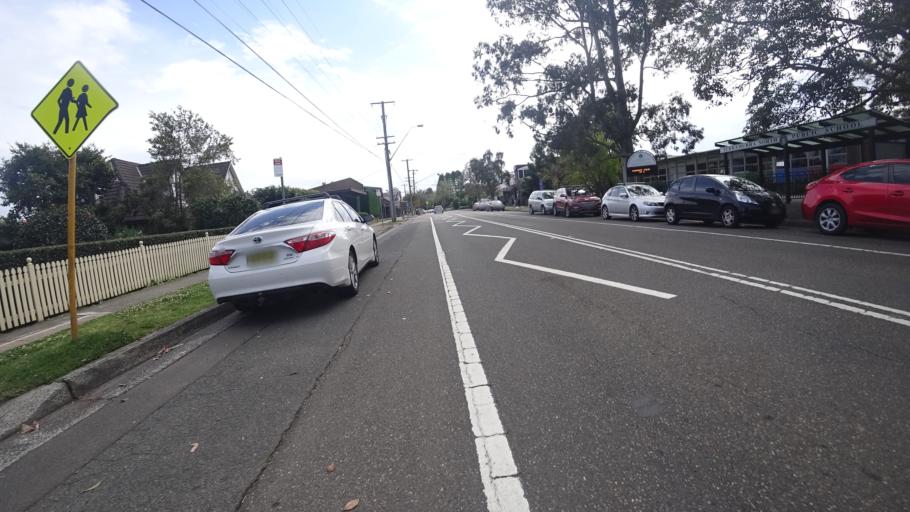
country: AU
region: New South Wales
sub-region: City of Sydney
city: North Turramurra
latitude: -33.7143
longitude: 151.1468
